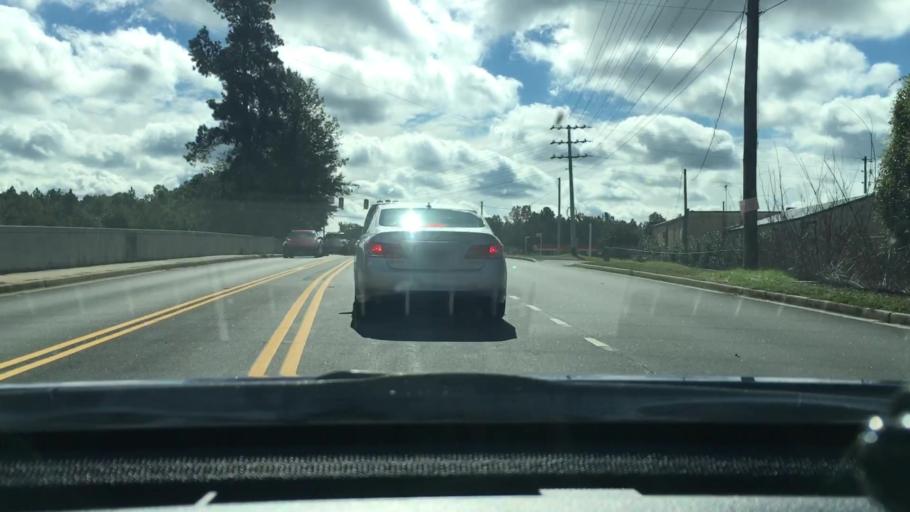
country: US
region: South Carolina
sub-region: Lexington County
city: Seven Oaks
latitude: 34.0676
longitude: -81.1461
